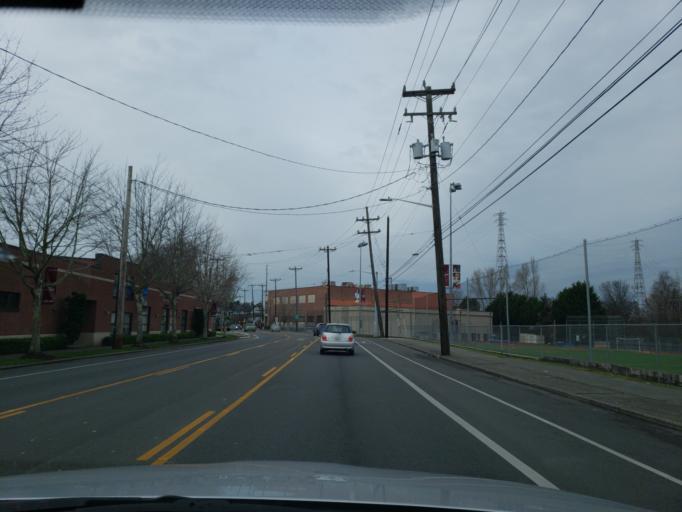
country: US
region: Washington
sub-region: King County
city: Seattle
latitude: 47.6501
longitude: -122.3583
